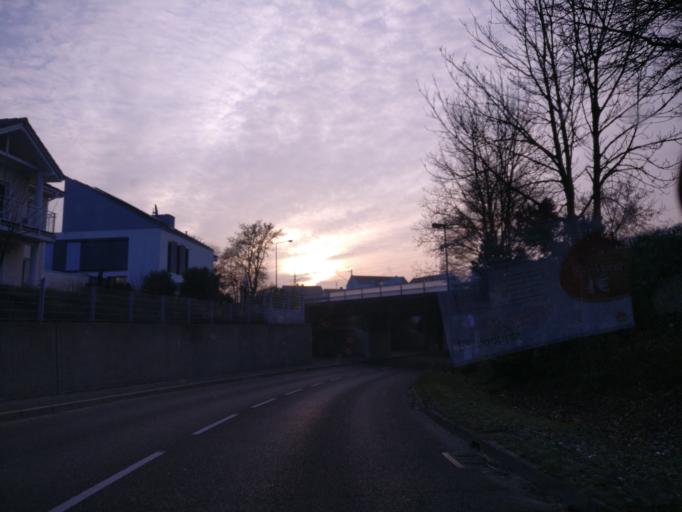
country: DE
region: Baden-Wuerttemberg
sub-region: Regierungsbezirk Stuttgart
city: Lorch
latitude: 48.7993
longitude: 9.6830
